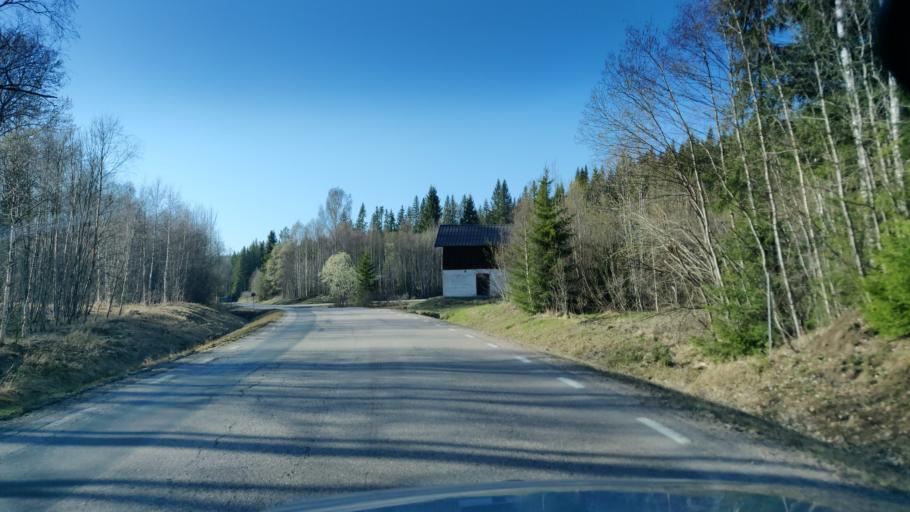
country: SE
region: Vaermland
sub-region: Munkfors Kommun
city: Munkfors
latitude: 59.9831
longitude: 13.4030
